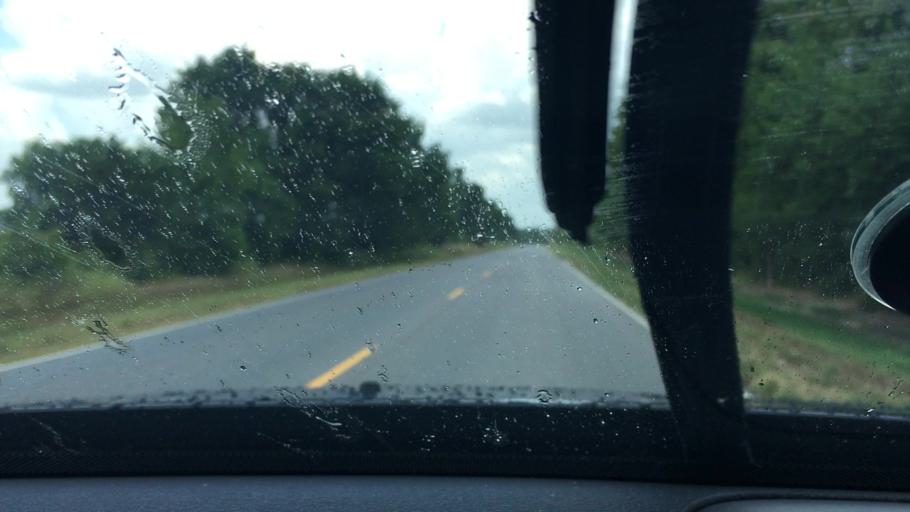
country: US
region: Oklahoma
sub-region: Johnston County
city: Tishomingo
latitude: 34.2064
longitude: -96.7098
